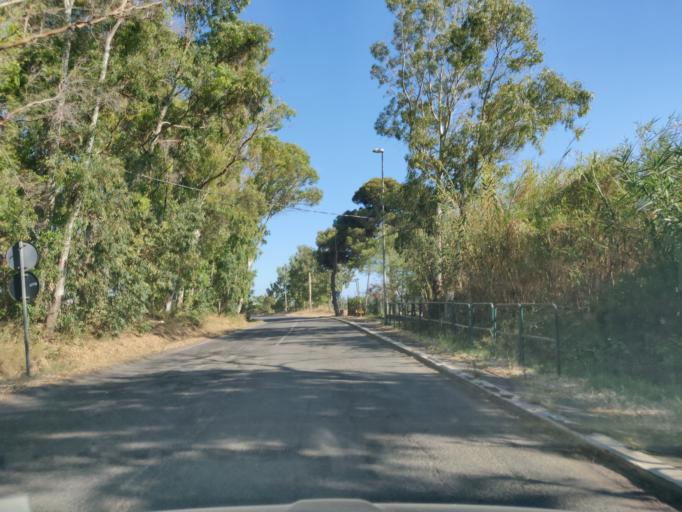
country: IT
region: Latium
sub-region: Citta metropolitana di Roma Capitale
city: Aurelia
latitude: 42.1322
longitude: 11.7719
